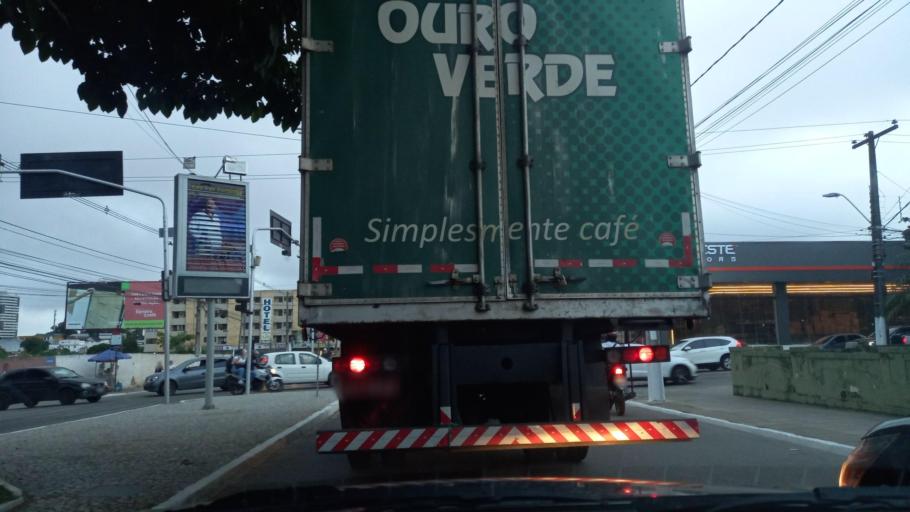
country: BR
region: Pernambuco
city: Garanhuns
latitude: -8.8829
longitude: -36.4790
